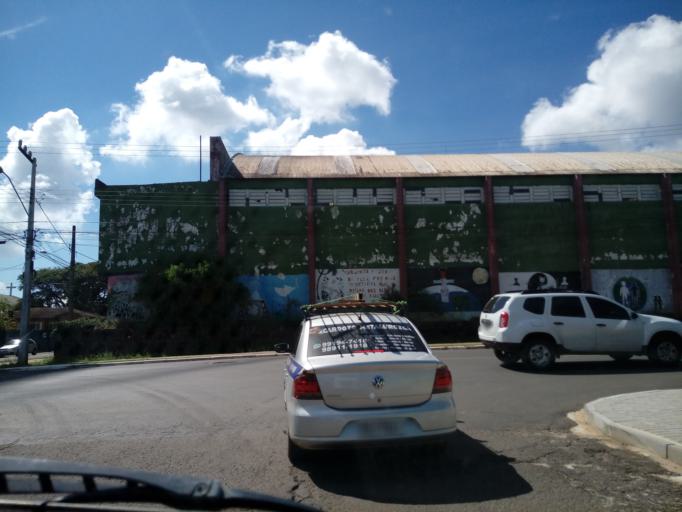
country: BR
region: Santa Catarina
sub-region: Chapeco
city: Chapeco
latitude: -27.0918
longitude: -52.6114
